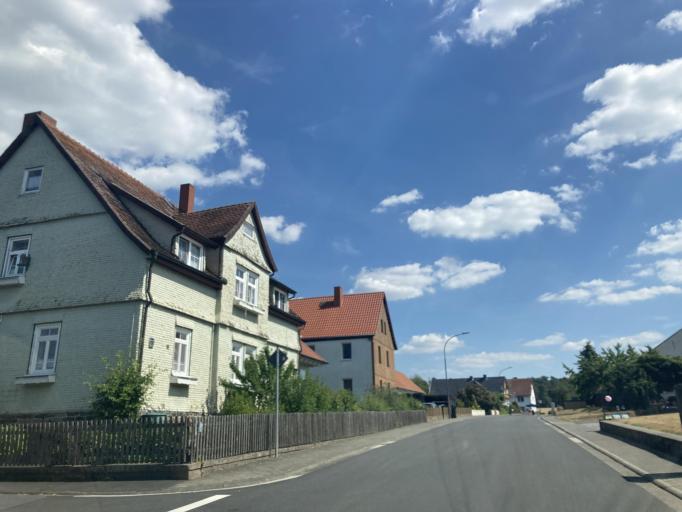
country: DE
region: Hesse
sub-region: Regierungsbezirk Giessen
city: Lauterbach
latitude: 50.6763
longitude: 9.4228
